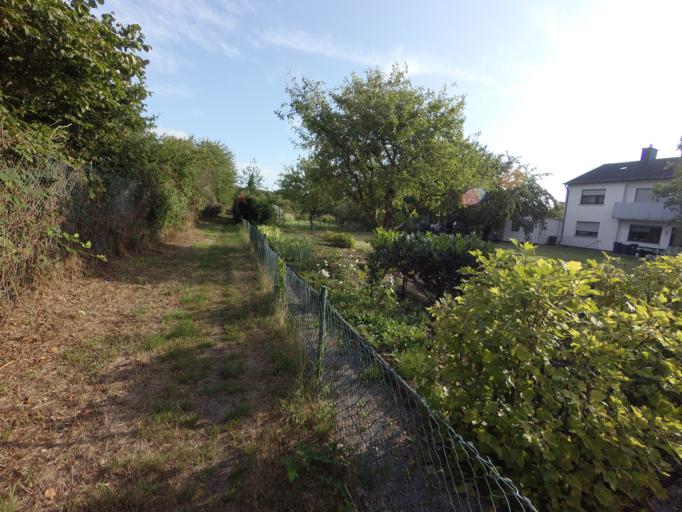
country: DE
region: North Rhine-Westphalia
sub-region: Regierungsbezirk Koln
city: Alsdorf
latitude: 50.8482
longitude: 6.1765
